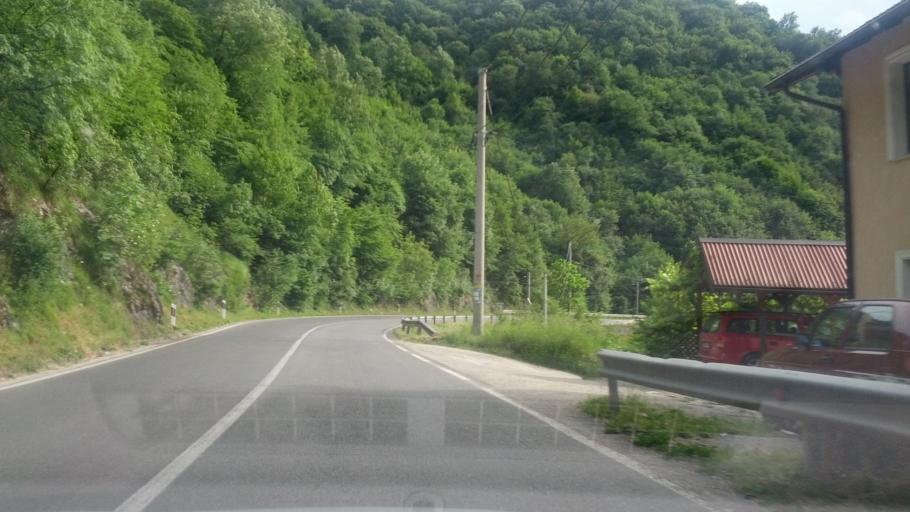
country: BA
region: Federation of Bosnia and Herzegovina
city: Ostrozac
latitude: 44.8829
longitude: 15.9026
